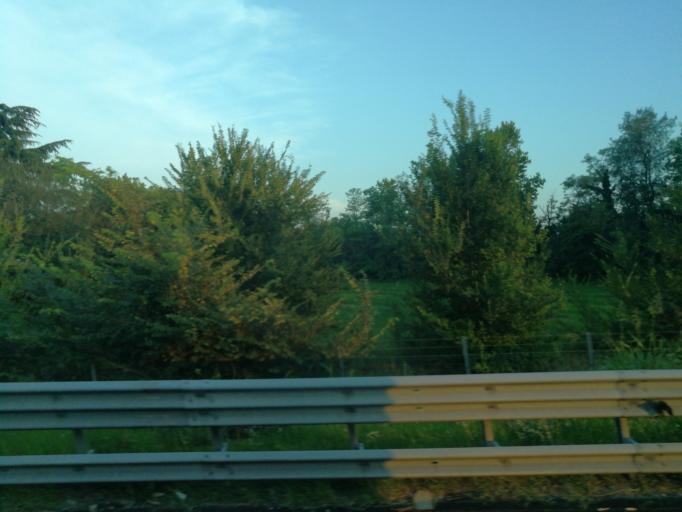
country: IT
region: Lombardy
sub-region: Provincia di Bergamo
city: Brembate
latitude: 45.6166
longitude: 9.5638
